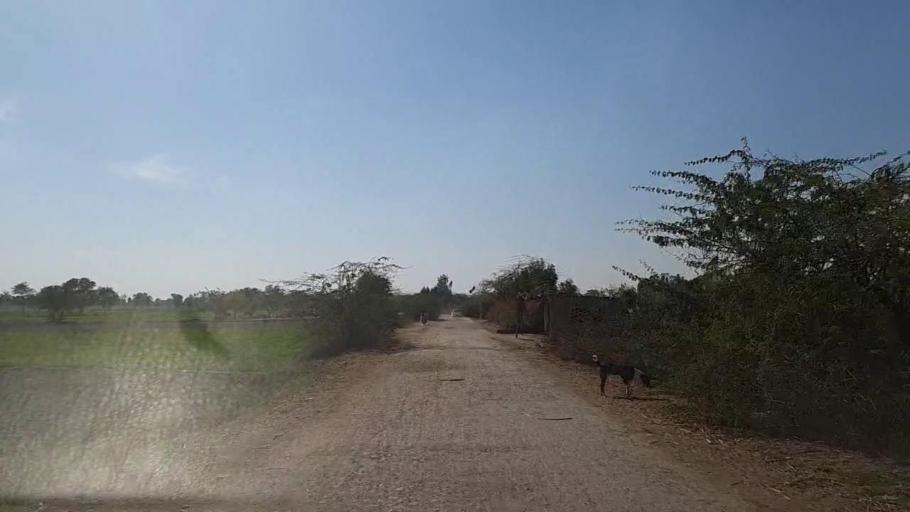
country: PK
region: Sindh
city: Nawabshah
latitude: 26.2242
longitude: 68.4277
